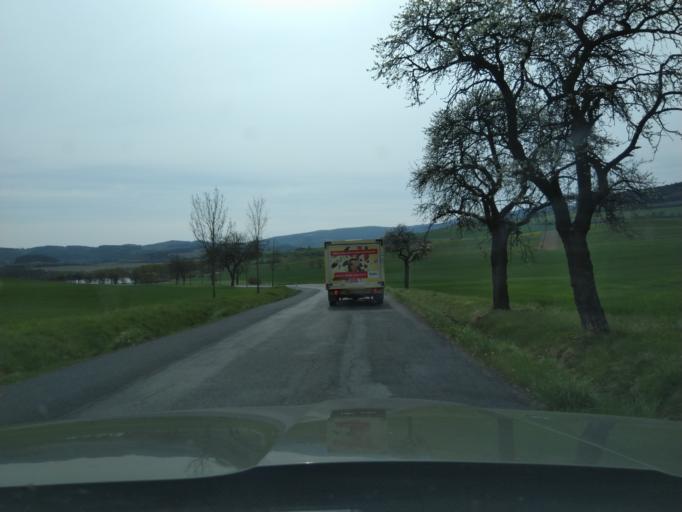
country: CZ
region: Plzensky
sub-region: Okres Klatovy
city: Susice
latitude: 49.2278
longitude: 13.5870
